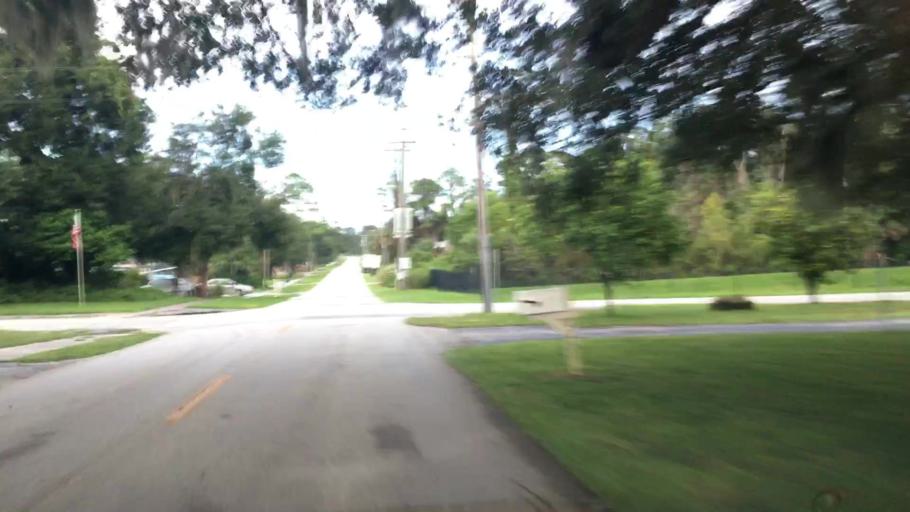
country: US
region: Florida
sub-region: Volusia County
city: DeBary
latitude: 28.8754
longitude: -81.2953
